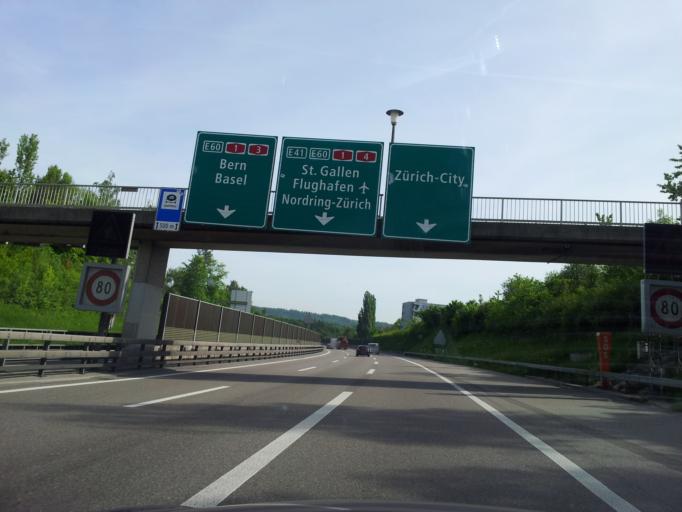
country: CH
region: Zurich
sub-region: Bezirk Dietikon
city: Dietikon / Hofacker
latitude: 47.3959
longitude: 8.4192
